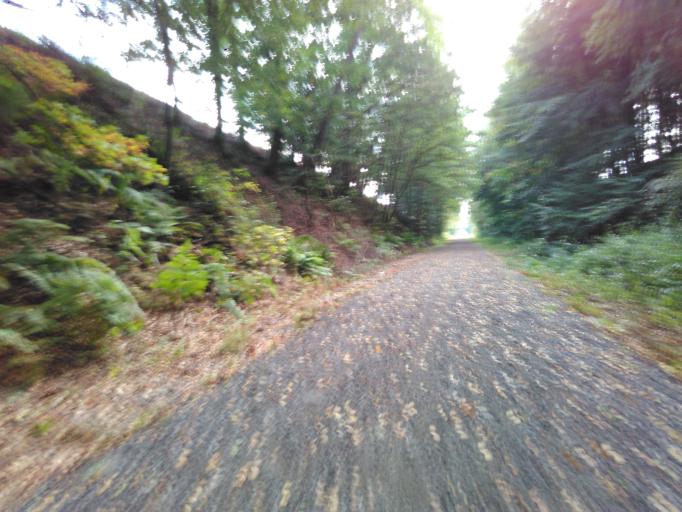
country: BE
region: Wallonia
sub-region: Province du Luxembourg
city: Neufchateau
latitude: 49.9129
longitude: 5.4368
